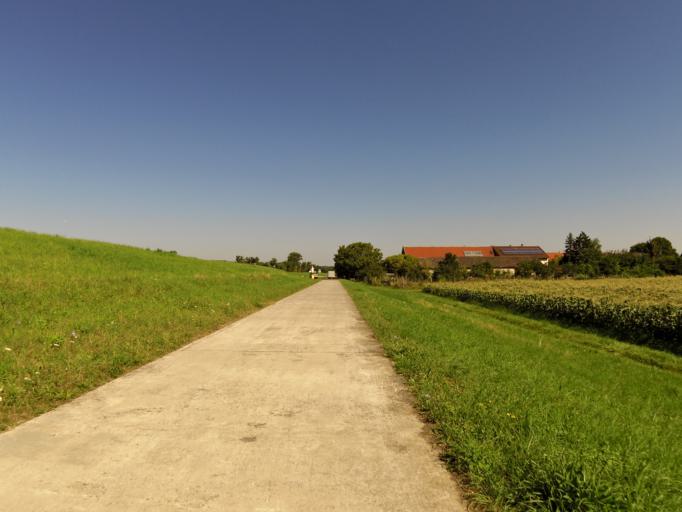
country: DE
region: Rheinland-Pfalz
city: Nierstein
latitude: 49.8875
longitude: 8.3591
